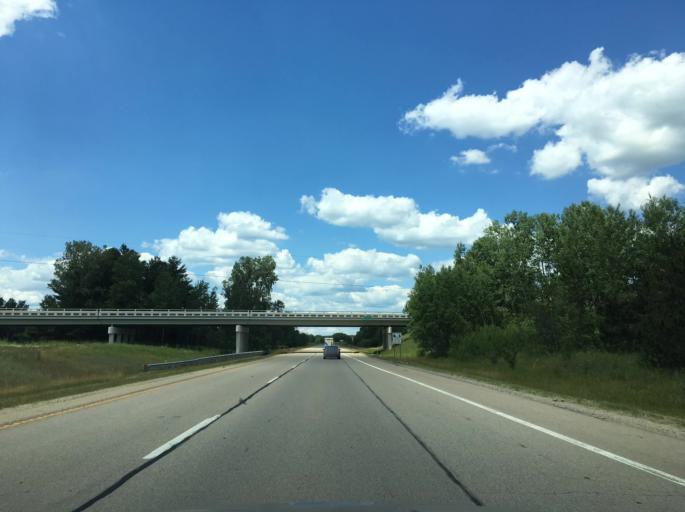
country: US
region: Michigan
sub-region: Clare County
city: Clare
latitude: 43.8812
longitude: -84.7867
